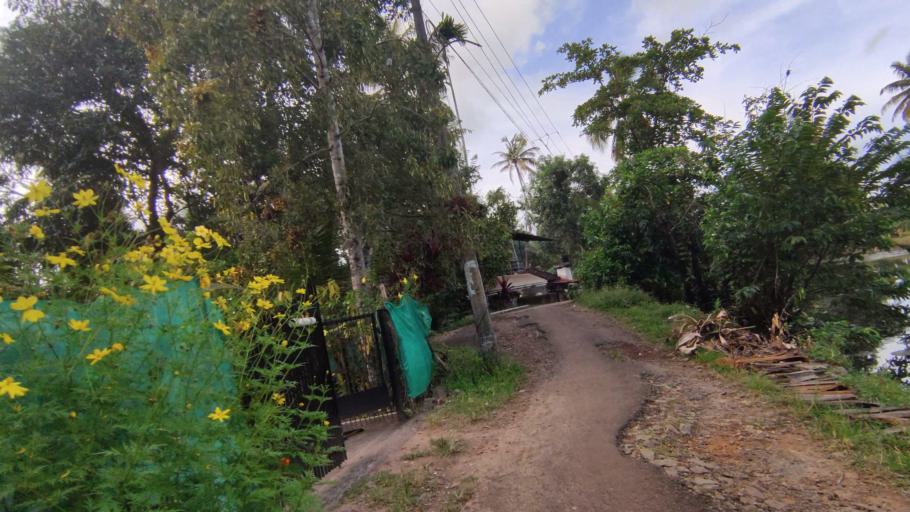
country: IN
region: Kerala
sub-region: Kottayam
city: Kottayam
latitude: 9.6008
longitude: 76.4397
